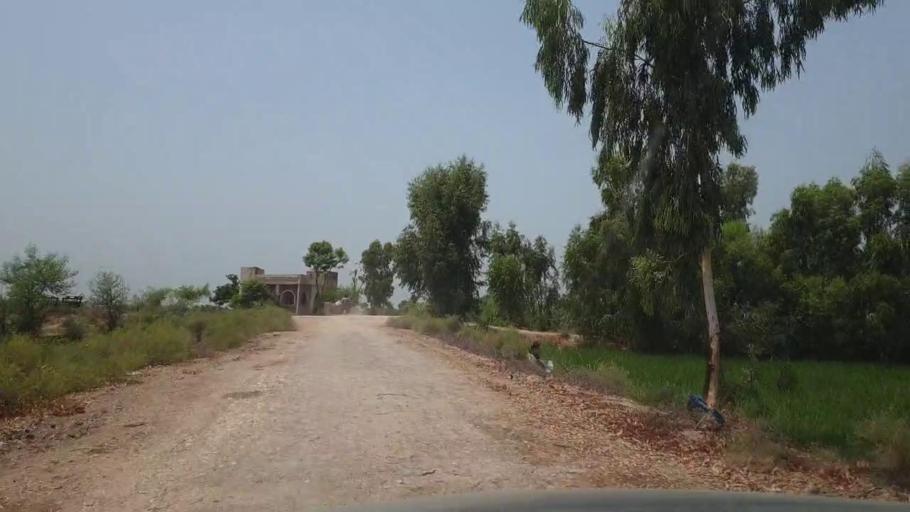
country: PK
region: Sindh
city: Garhi Yasin
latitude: 27.8870
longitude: 68.4306
